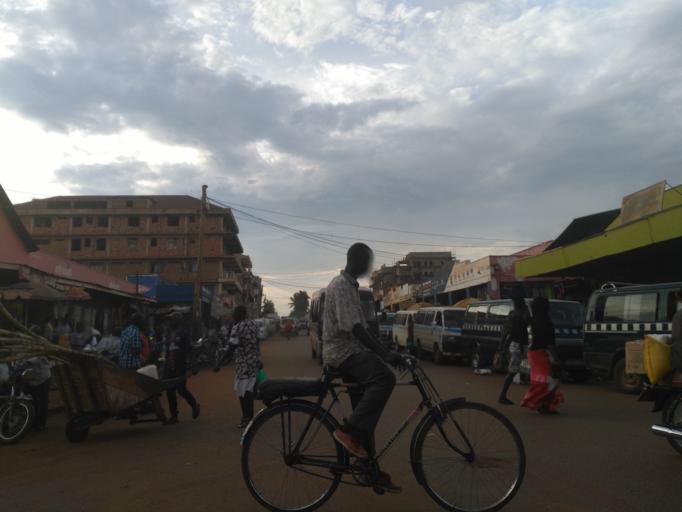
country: UG
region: Eastern Region
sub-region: Jinja District
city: Jinja
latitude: 0.4322
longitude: 33.2132
